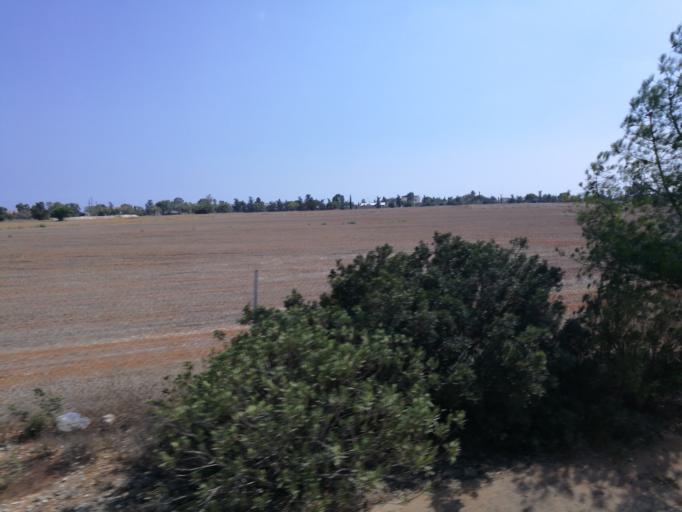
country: CY
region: Larnaka
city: Xylotymbou
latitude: 35.0063
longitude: 33.7321
